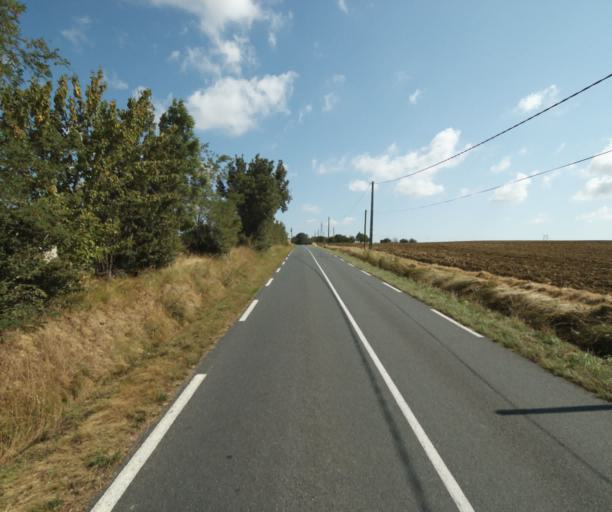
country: FR
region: Midi-Pyrenees
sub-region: Departement de la Haute-Garonne
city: Auriac-sur-Vendinelle
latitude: 43.4523
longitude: 1.8155
